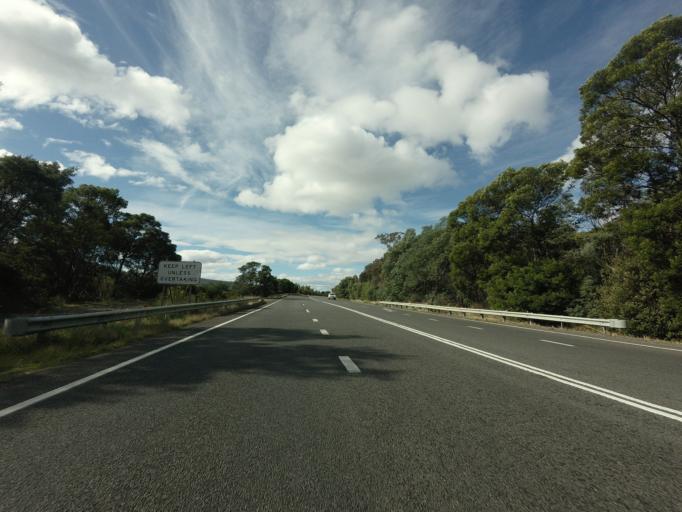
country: AU
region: Tasmania
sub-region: Glenorchy
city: Granton
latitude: -42.7546
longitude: 147.1619
